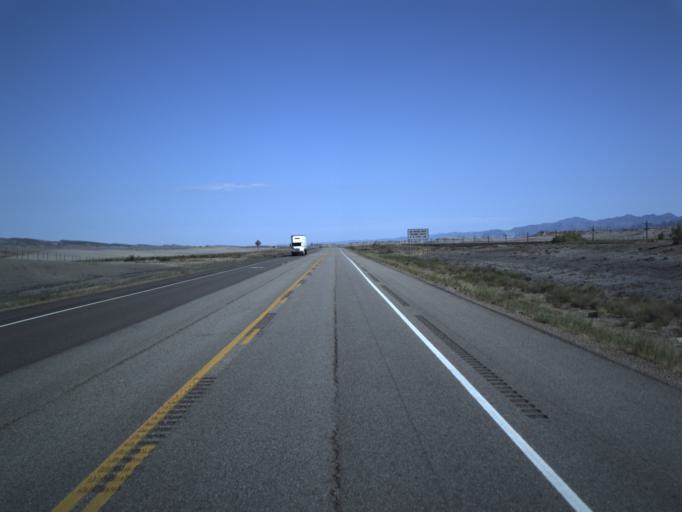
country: US
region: Utah
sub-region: Carbon County
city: East Carbon City
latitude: 39.1067
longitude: -110.3256
